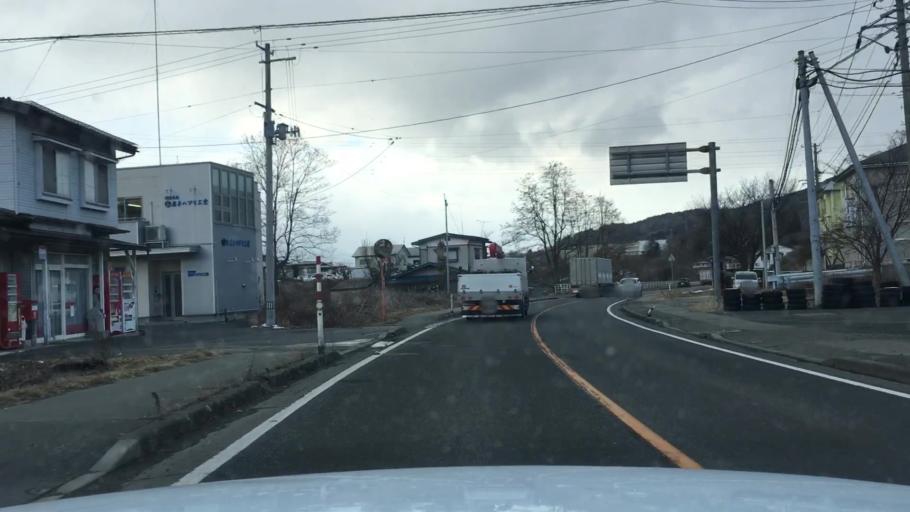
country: JP
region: Iwate
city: Morioka-shi
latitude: 39.6820
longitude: 141.1828
